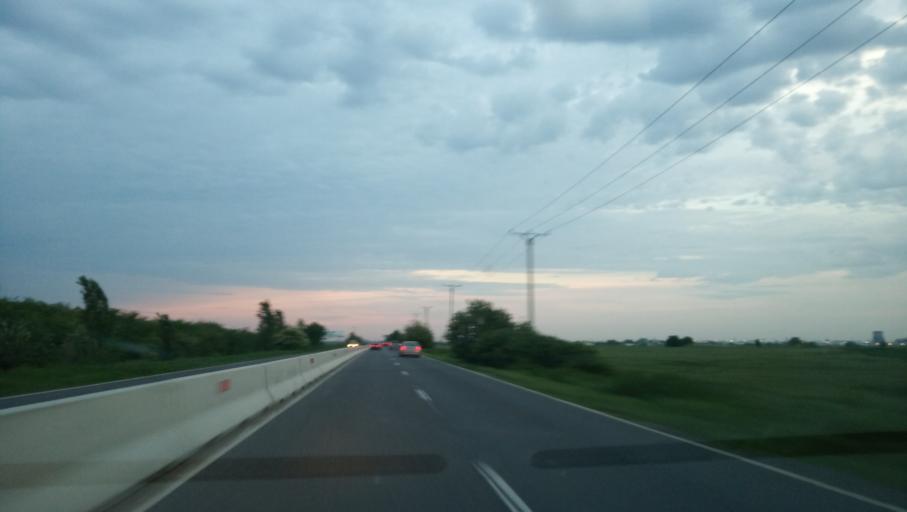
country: RO
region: Timis
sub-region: Comuna Sag
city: Sag
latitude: 45.6770
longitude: 21.1700
